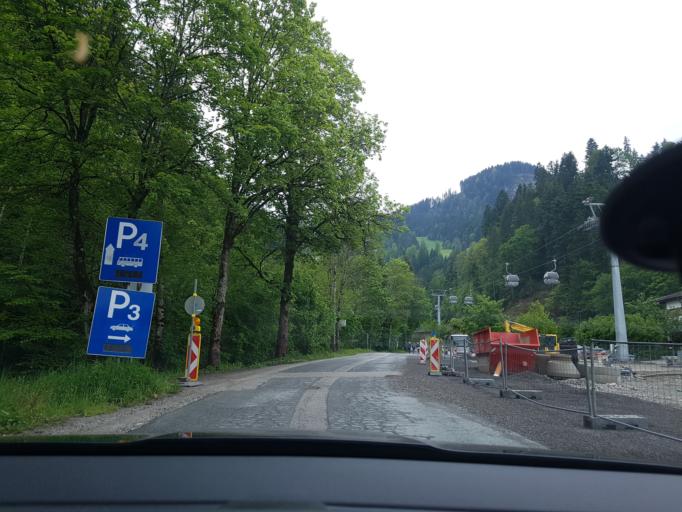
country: AT
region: Tyrol
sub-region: Politischer Bezirk Kufstein
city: Soll
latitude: 47.4966
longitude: 12.1987
